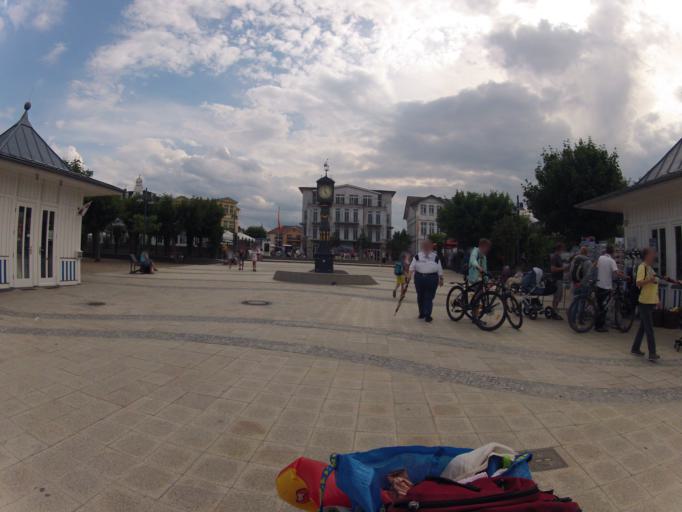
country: DE
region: Mecklenburg-Vorpommern
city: Seebad Heringsdorf
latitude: 53.9425
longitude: 14.1906
